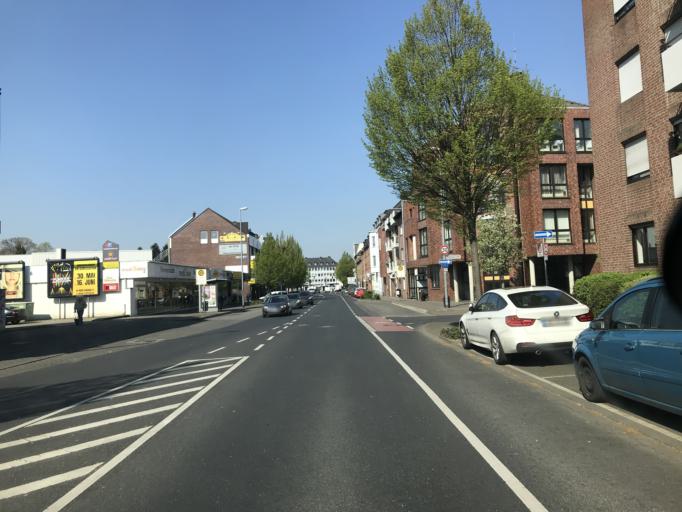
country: DE
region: North Rhine-Westphalia
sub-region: Regierungsbezirk Dusseldorf
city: Monchengladbach
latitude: 51.1821
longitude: 6.4404
